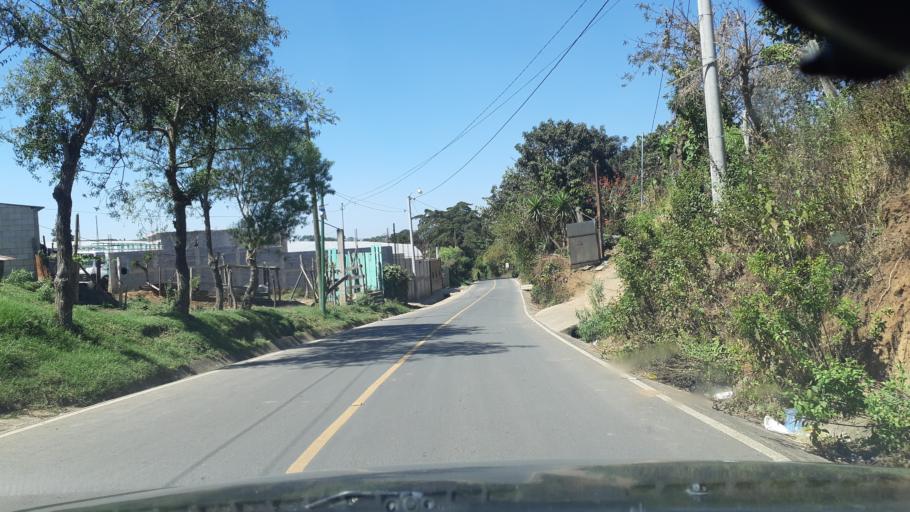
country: GT
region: Chimaltenango
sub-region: Municipio de Zaragoza
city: Zaragoza
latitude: 14.6593
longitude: -90.8642
